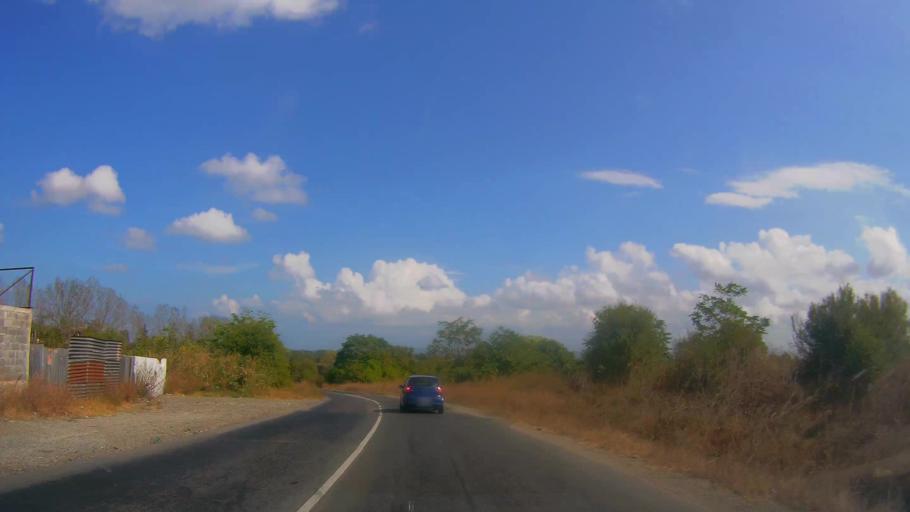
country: BG
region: Burgas
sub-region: Obshtina Burgas
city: Burgas
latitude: 42.4735
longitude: 27.4192
